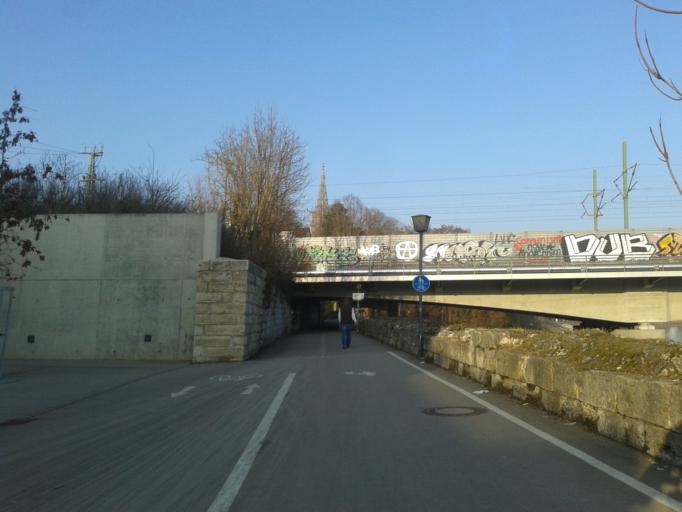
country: DE
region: Baden-Wuerttemberg
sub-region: Tuebingen Region
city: Ulm
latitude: 48.3928
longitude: 9.9877
